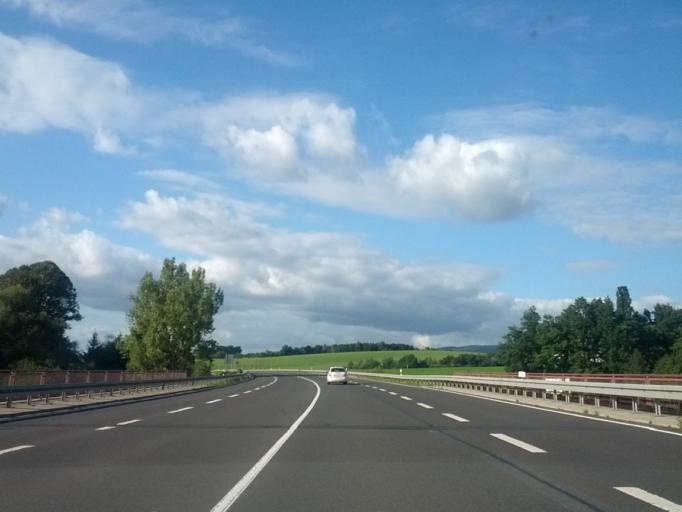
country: DE
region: Thuringia
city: Barchfeld
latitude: 50.8008
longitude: 10.3224
